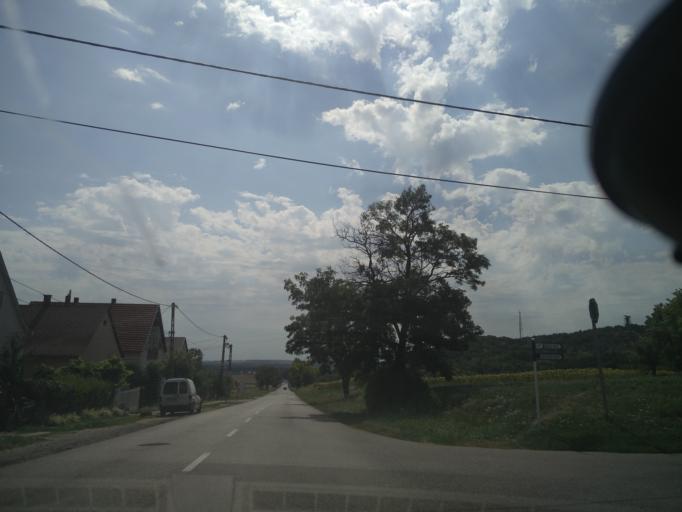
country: HU
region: Fejer
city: Velence
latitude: 47.2572
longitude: 18.6214
